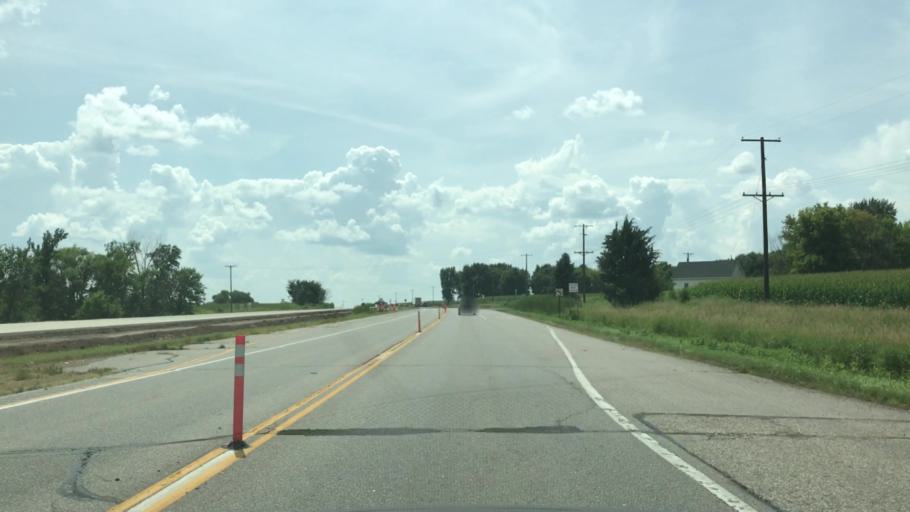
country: US
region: Minnesota
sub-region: Scott County
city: Belle Plaine
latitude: 44.5874
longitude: -93.8276
